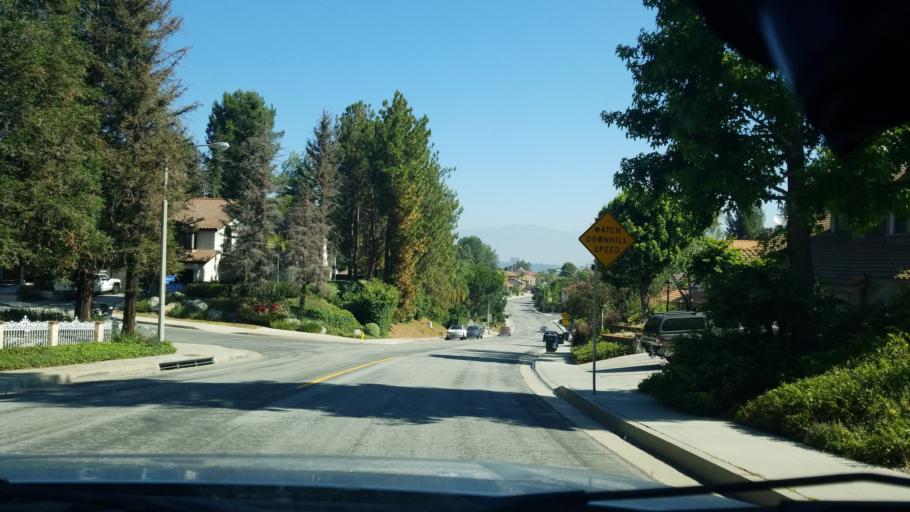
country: US
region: California
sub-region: Los Angeles County
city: Rowland Heights
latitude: 33.9782
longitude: -117.9257
